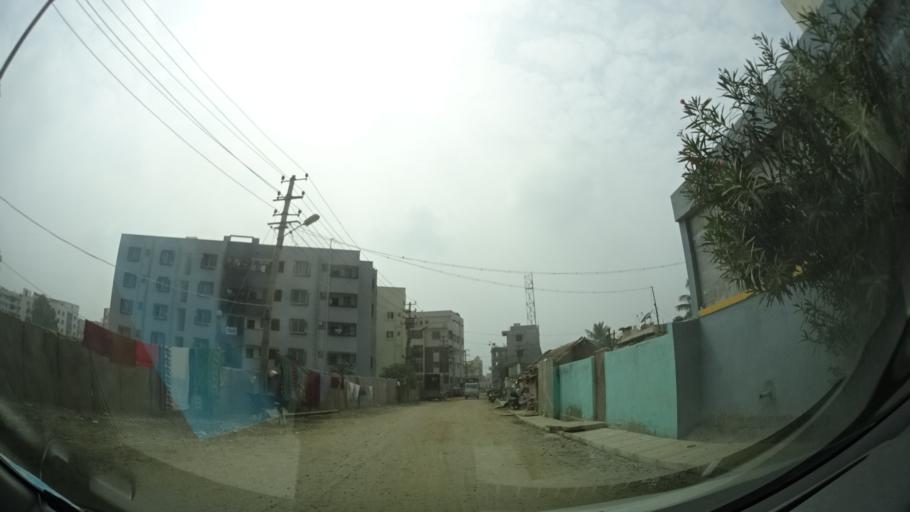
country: IN
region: Karnataka
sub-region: Bangalore Rural
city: Hoskote
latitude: 12.9766
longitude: 77.7570
